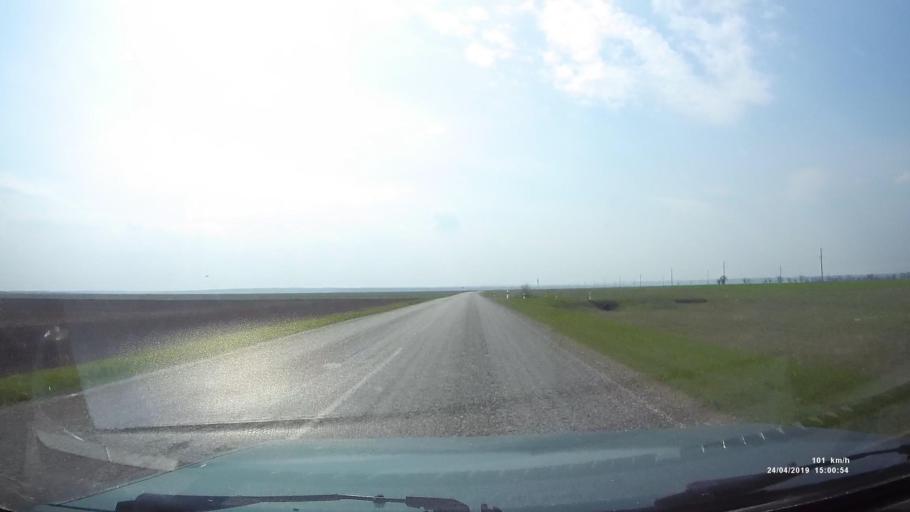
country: RU
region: Rostov
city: Remontnoye
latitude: 46.5655
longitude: 43.5453
